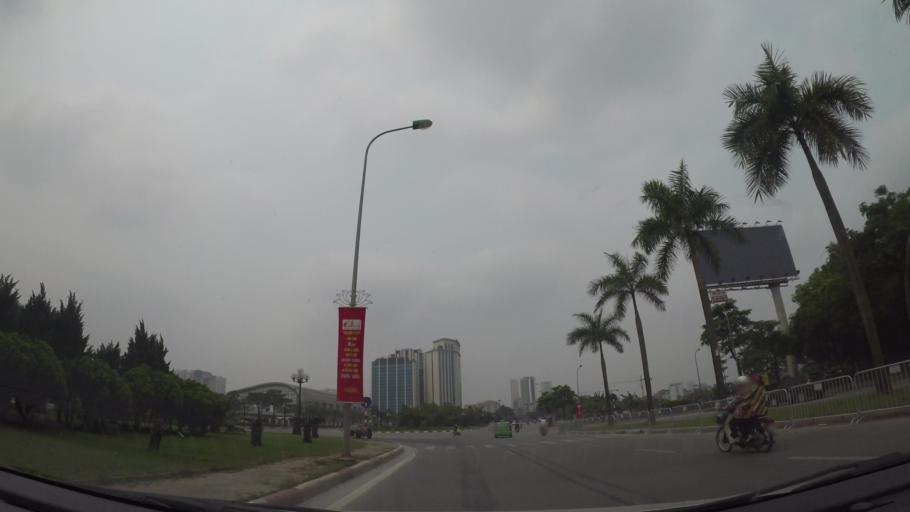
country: VN
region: Ha Noi
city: Cau Dien
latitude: 21.0233
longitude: 105.7670
